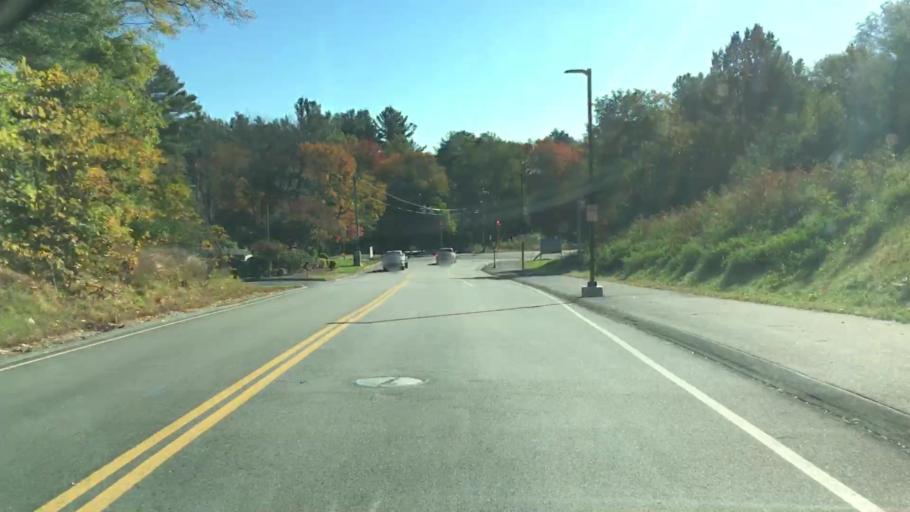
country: US
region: Massachusetts
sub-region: Middlesex County
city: Ashland
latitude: 42.2535
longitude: -71.4710
